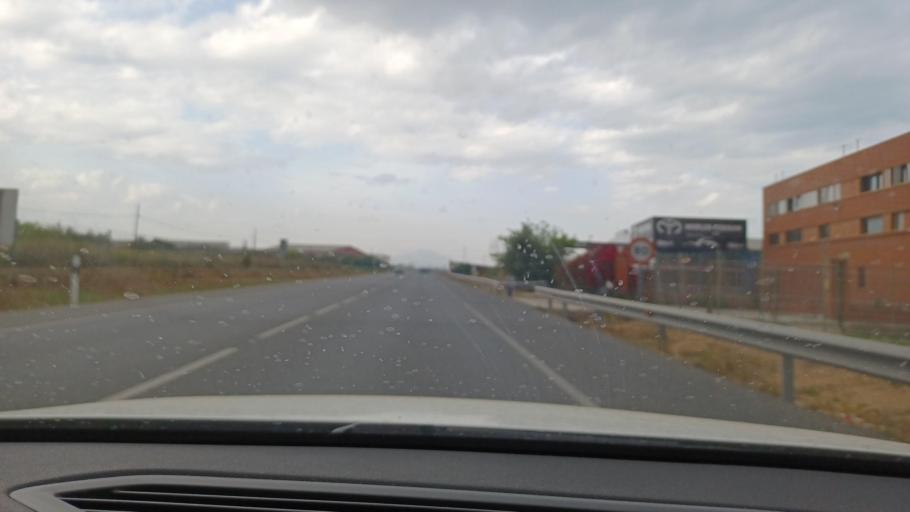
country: ES
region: Valencia
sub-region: Provincia de Castello
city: Benicarlo
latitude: 40.4352
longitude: 0.4393
